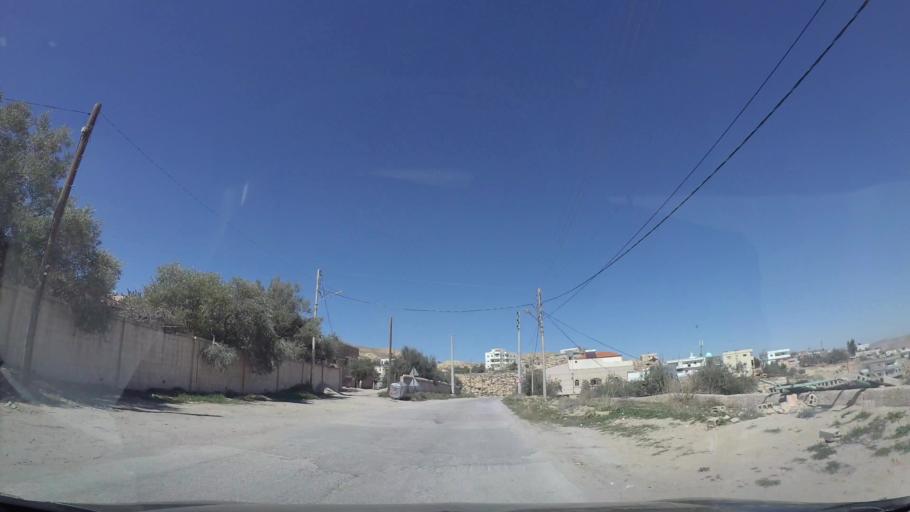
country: JO
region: Tafielah
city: At Tafilah
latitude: 30.8236
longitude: 35.5807
